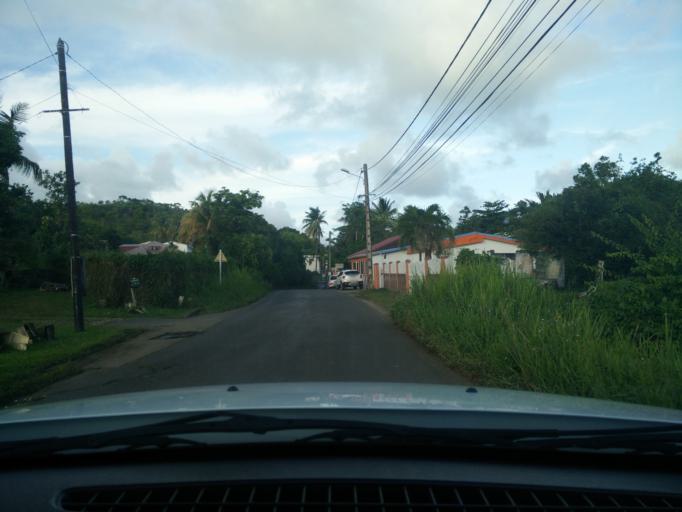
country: GP
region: Guadeloupe
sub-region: Guadeloupe
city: Les Abymes
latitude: 16.2545
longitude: -61.5025
